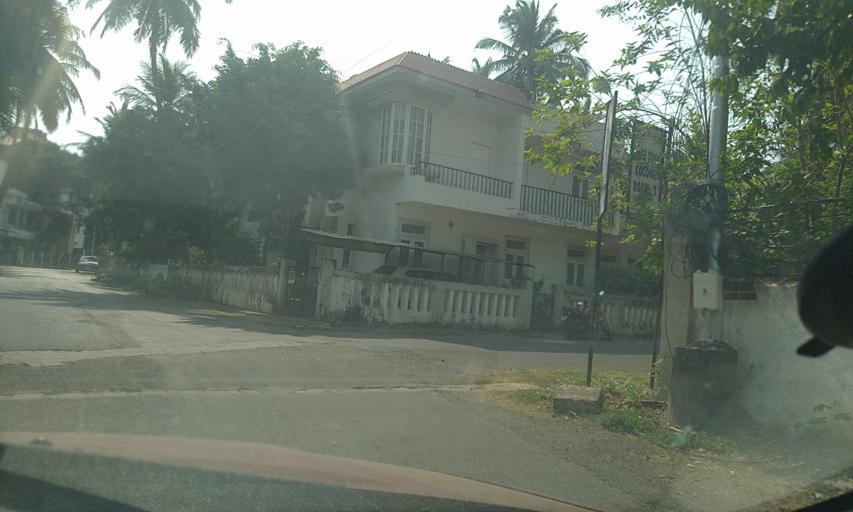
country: IN
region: Goa
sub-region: North Goa
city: Panaji
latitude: 15.4871
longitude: 73.8149
